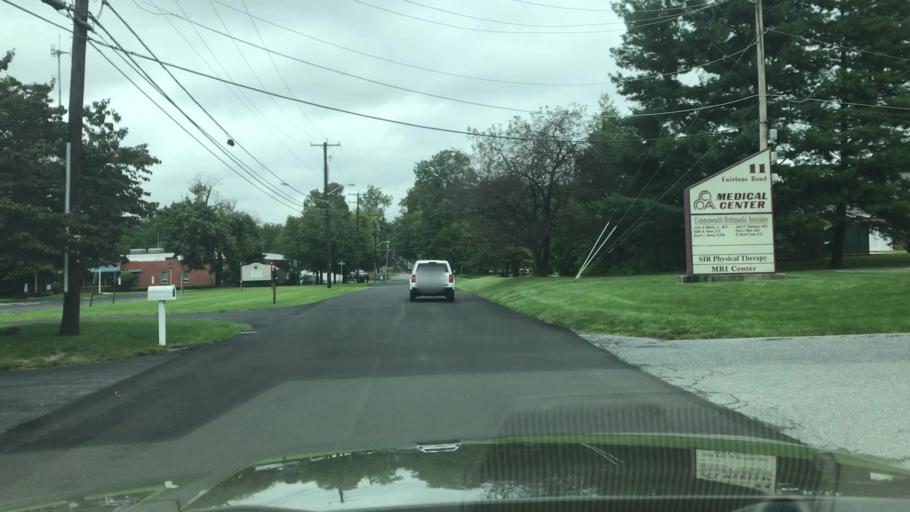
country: US
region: Pennsylvania
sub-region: Berks County
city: Lorane
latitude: 40.3035
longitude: -75.8536
